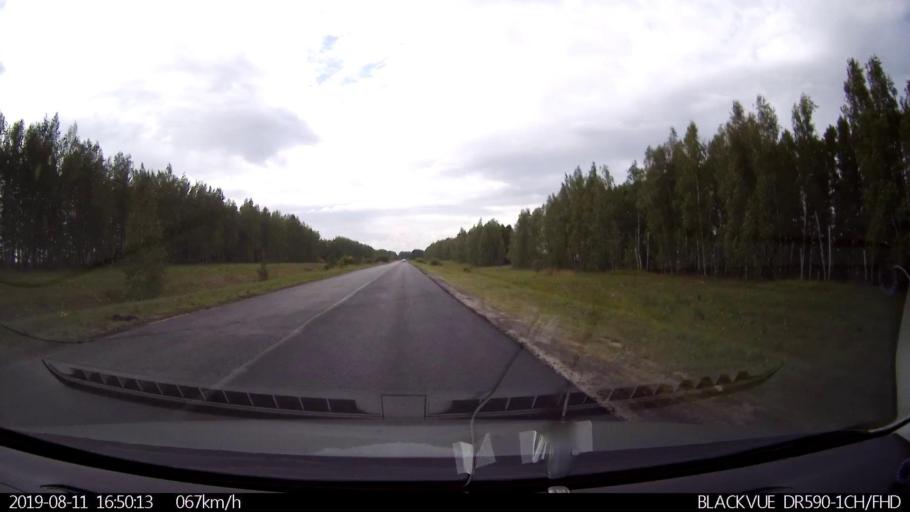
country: RU
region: Ulyanovsk
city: Mayna
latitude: 54.2268
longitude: 47.6899
